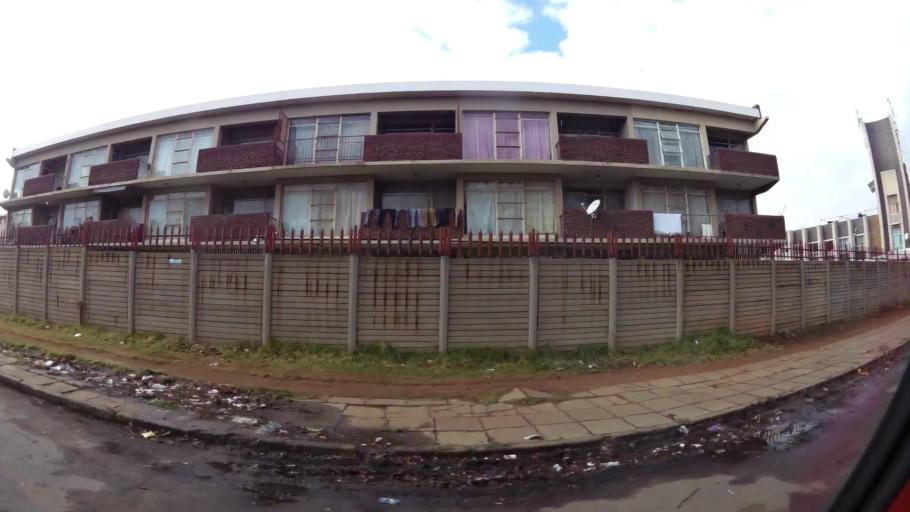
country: ZA
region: Gauteng
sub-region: Sedibeng District Municipality
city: Vanderbijlpark
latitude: -26.6936
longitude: 27.8257
